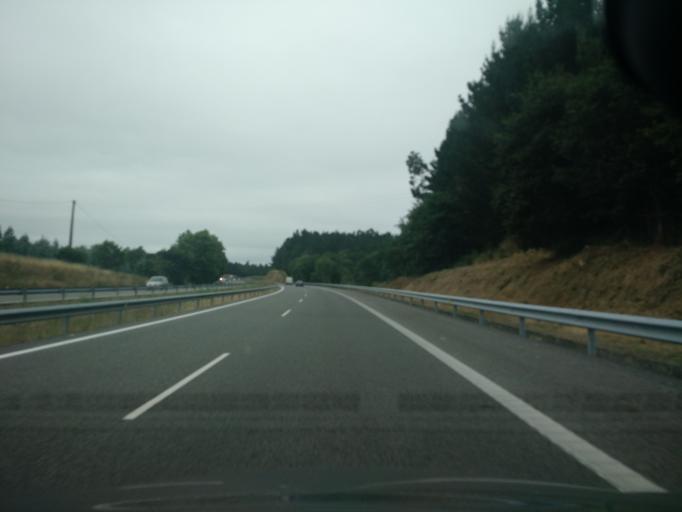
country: ES
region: Galicia
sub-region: Provincia da Coruna
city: Oroso
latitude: 43.0105
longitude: -8.4193
